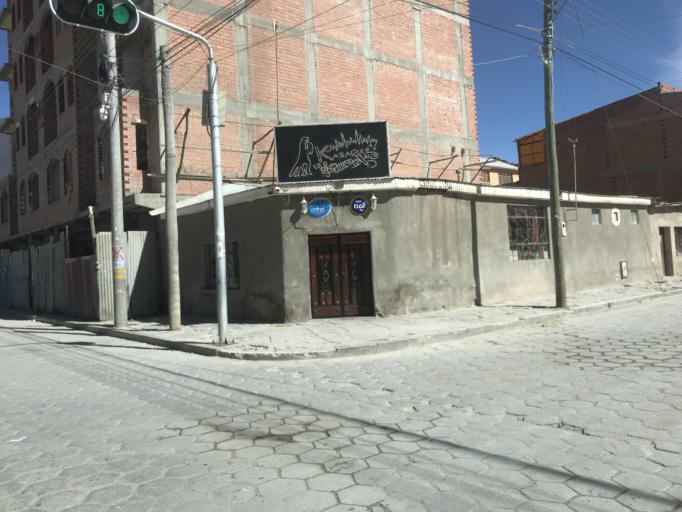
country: BO
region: Potosi
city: Uyuni
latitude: -20.4604
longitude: -66.8234
